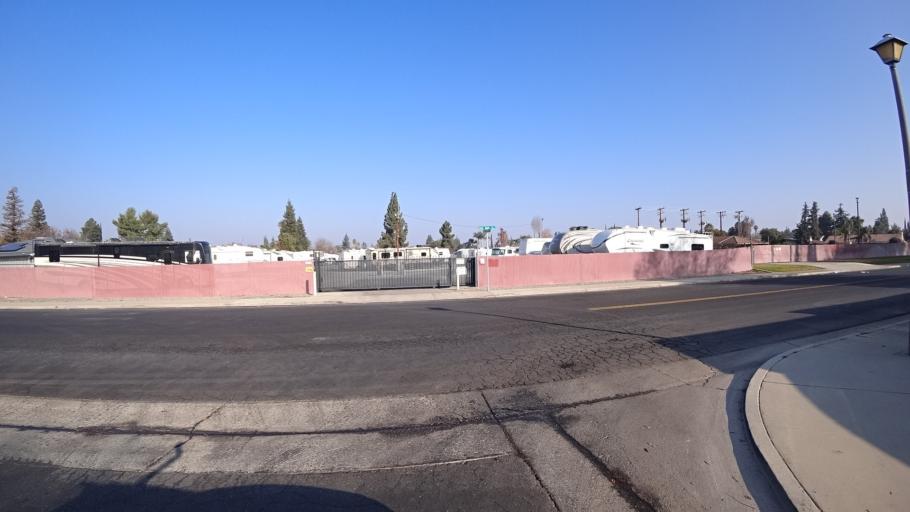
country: US
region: California
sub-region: Kern County
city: Greenacres
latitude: 35.3396
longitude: -119.0756
